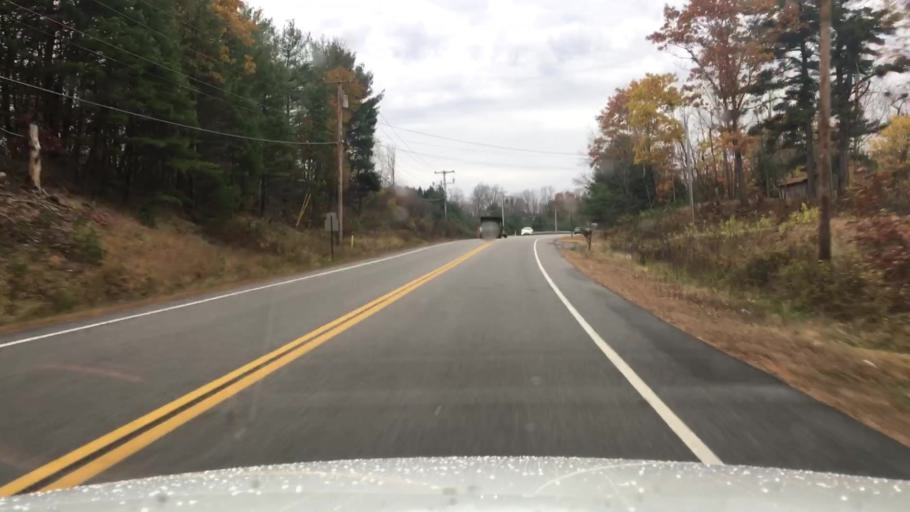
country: US
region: Maine
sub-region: Kennebec County
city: Pittston
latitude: 44.2215
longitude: -69.7571
